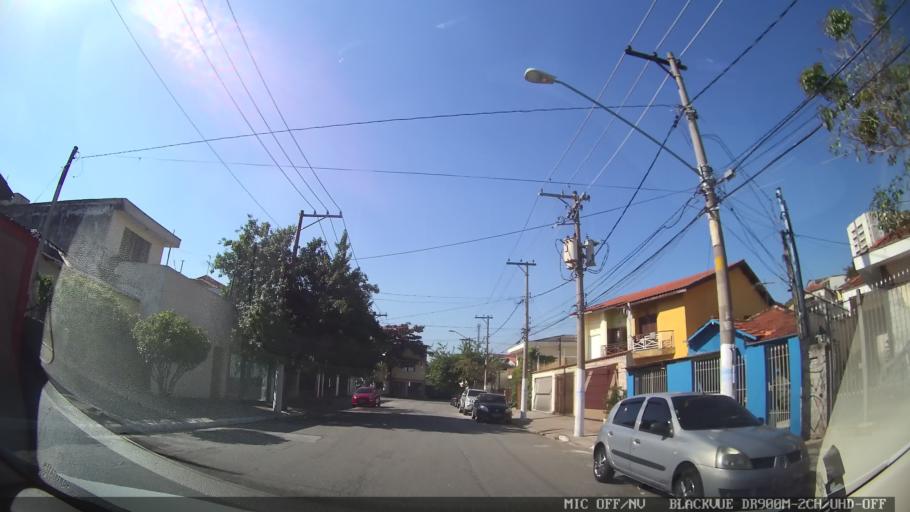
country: BR
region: Sao Paulo
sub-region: Sao Paulo
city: Sao Paulo
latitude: -23.5035
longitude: -46.6639
